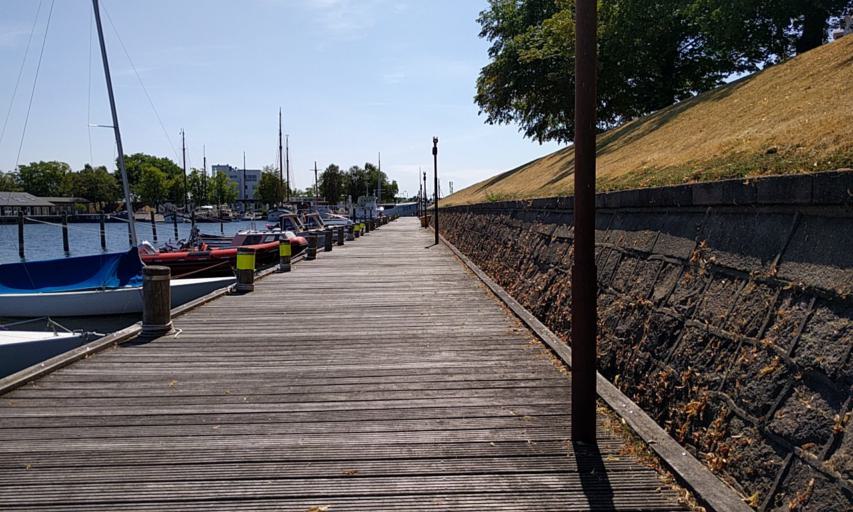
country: DK
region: Capital Region
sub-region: Kobenhavn
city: Christianshavn
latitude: 55.6889
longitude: 12.6079
